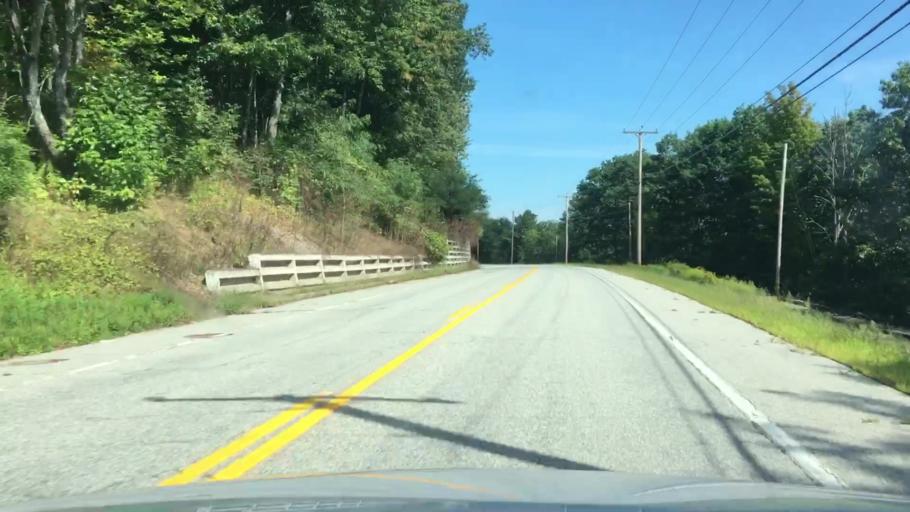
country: US
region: Maine
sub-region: Kennebec County
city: Pittston
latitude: 44.2136
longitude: -69.7627
